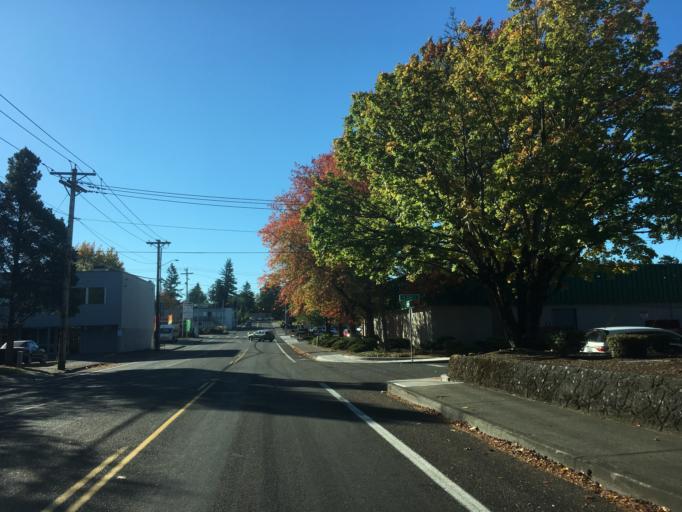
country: US
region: Oregon
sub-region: Multnomah County
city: Gresham
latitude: 45.4993
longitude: -122.4210
